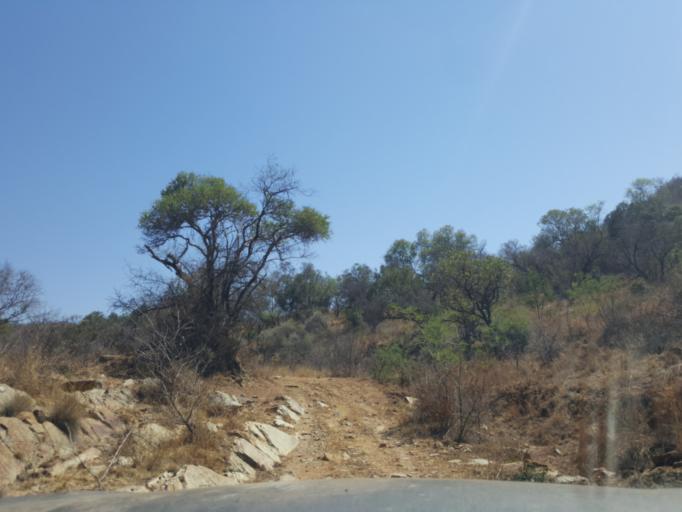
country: BW
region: South East
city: Lobatse
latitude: -25.1494
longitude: 25.6708
